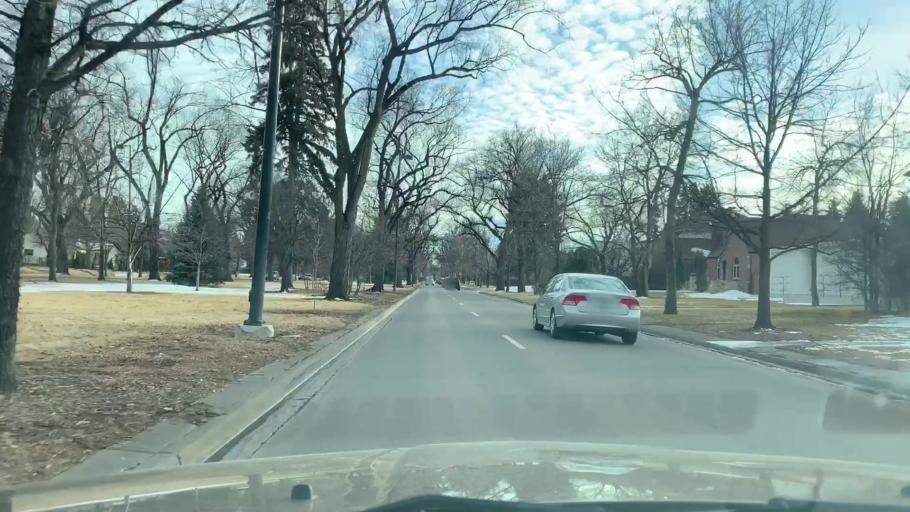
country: US
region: Colorado
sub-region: Arapahoe County
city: Glendale
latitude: 39.7314
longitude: -104.9128
